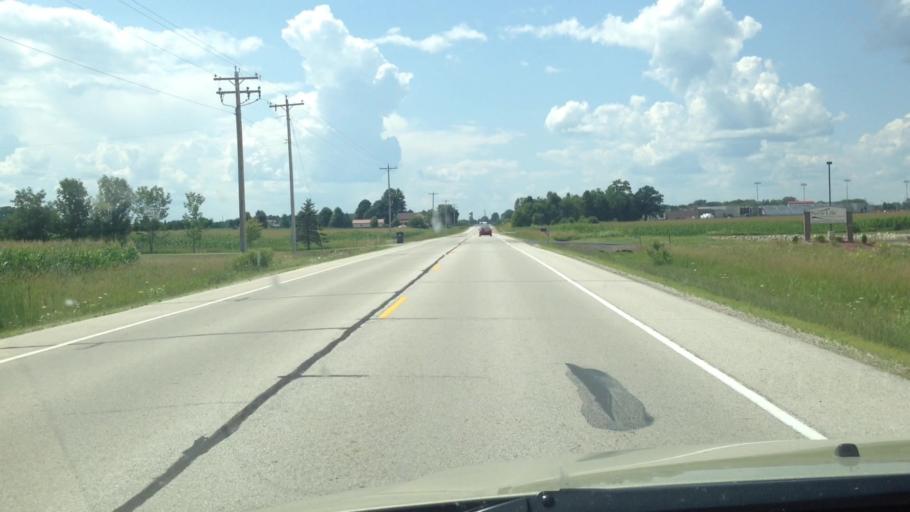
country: US
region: Wisconsin
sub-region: Brown County
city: Pulaski
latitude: 44.6570
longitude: -88.2274
